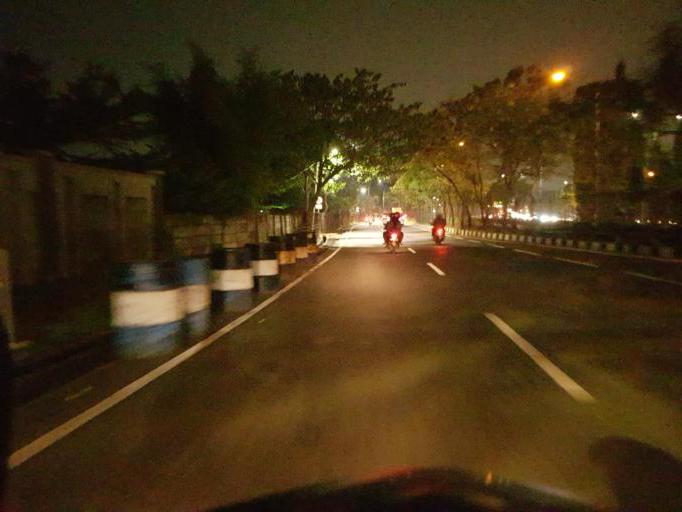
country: ID
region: West Java
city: Cileungsir
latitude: -6.3116
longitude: 106.9024
